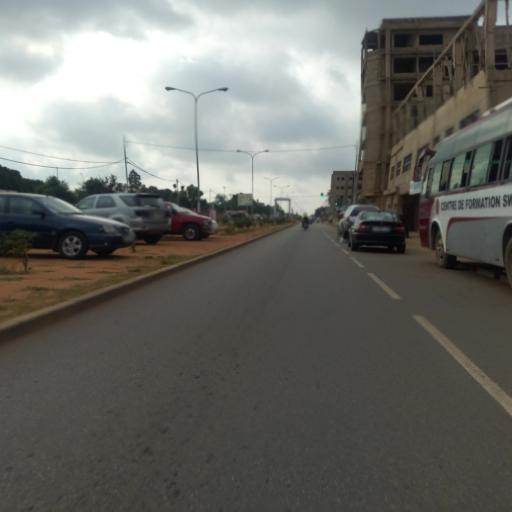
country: TG
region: Maritime
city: Lome
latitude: 6.1929
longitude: 1.2435
